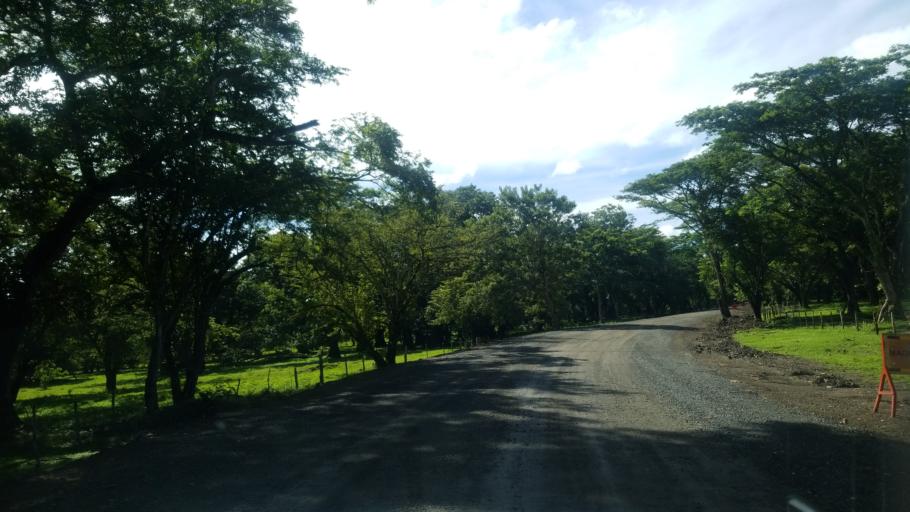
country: CR
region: Alajuela
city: San Jose
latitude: 11.1015
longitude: -85.2691
